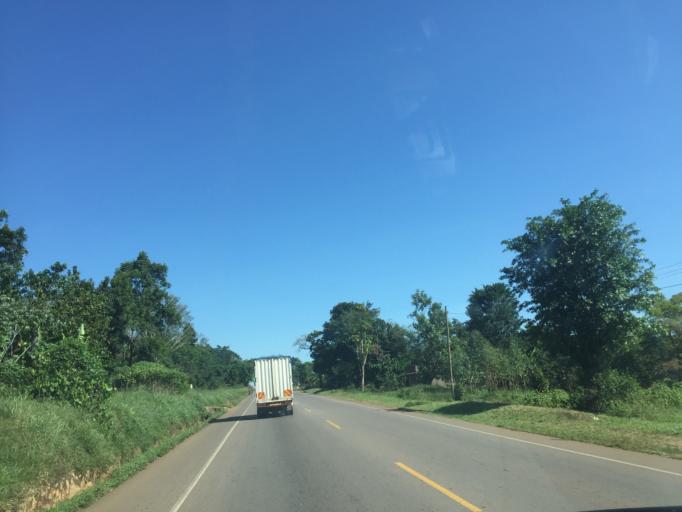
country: UG
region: Central Region
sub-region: Luwero District
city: Luwero
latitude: 0.7968
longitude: 32.5077
